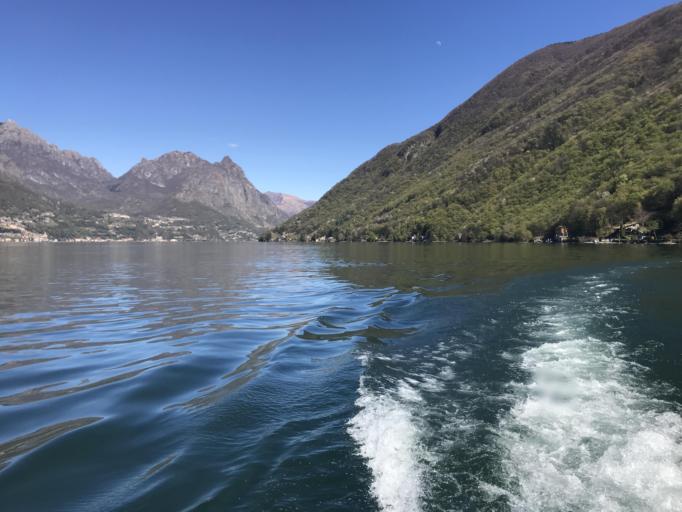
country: IT
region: Lombardy
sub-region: Provincia di Como
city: Lanzo d'Intelvi
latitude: 45.9991
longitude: 9.0134
